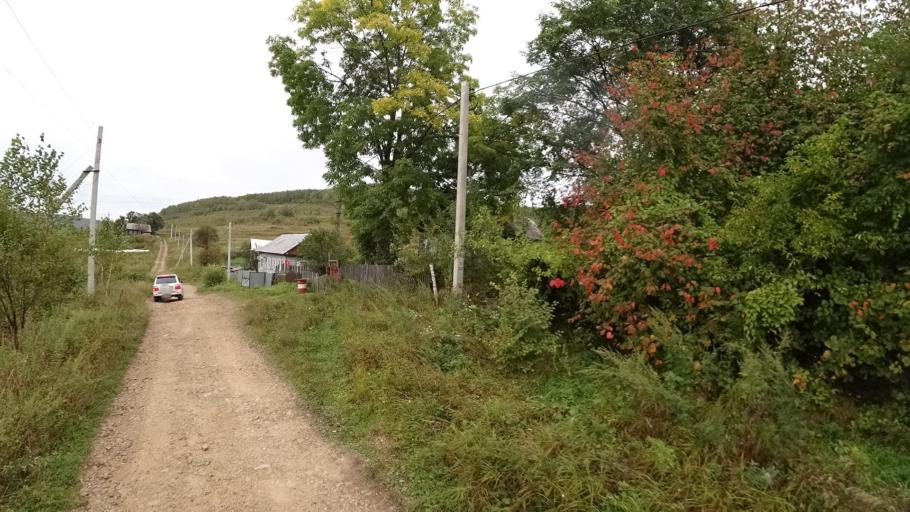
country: RU
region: Jewish Autonomous Oblast
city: Khingansk
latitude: 49.0373
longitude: 131.0606
